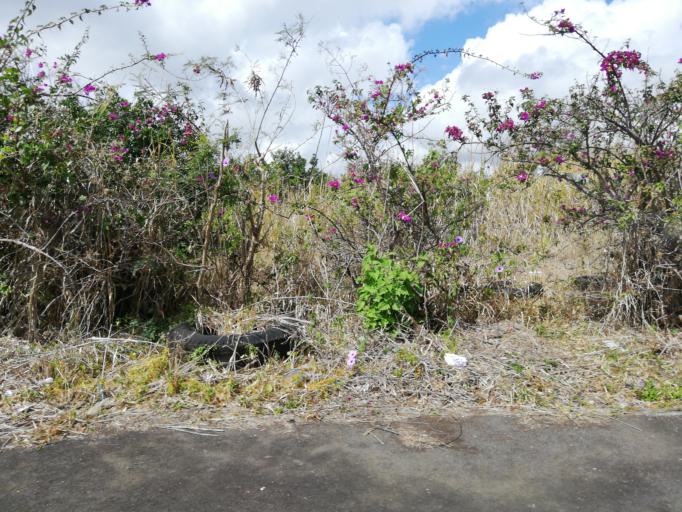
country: MU
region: Plaines Wilhems
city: Ebene
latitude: -20.2379
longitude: 57.4808
